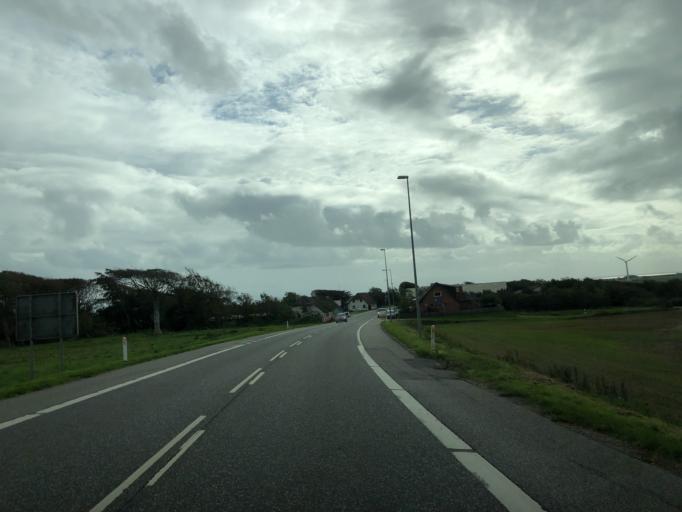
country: DK
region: North Denmark
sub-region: Thisted Kommune
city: Hurup
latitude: 56.7076
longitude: 8.4128
